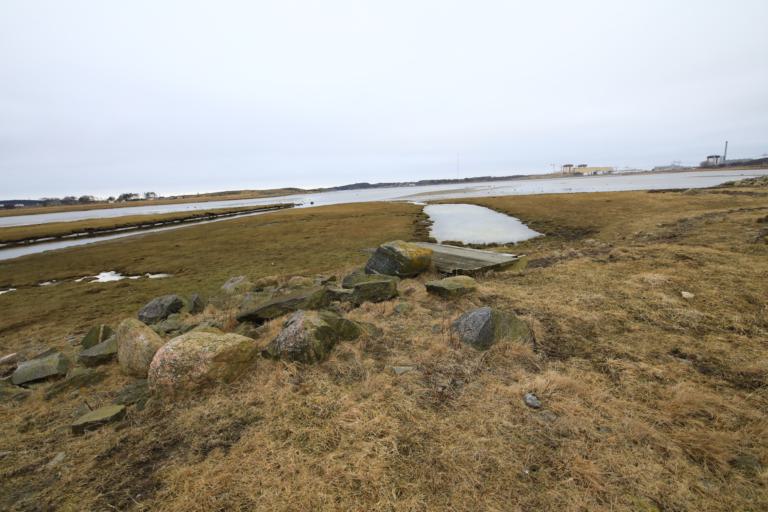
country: SE
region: Halland
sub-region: Kungsbacka Kommun
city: Frillesas
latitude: 57.2472
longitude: 12.1311
